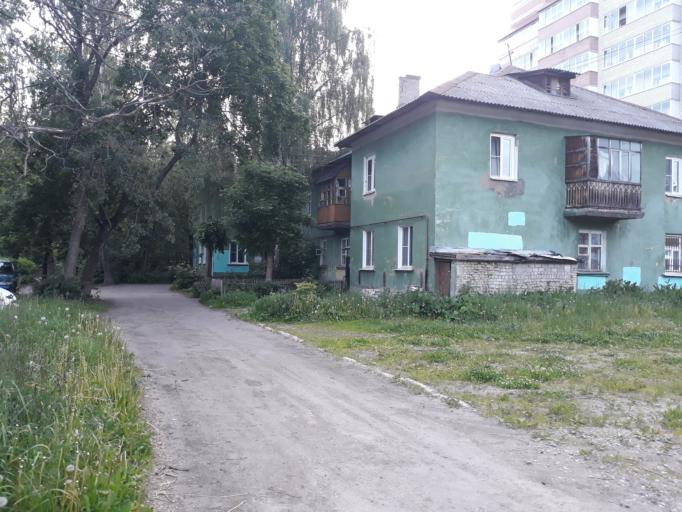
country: RU
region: Jaroslavl
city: Yaroslavl
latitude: 57.6412
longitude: 39.8314
